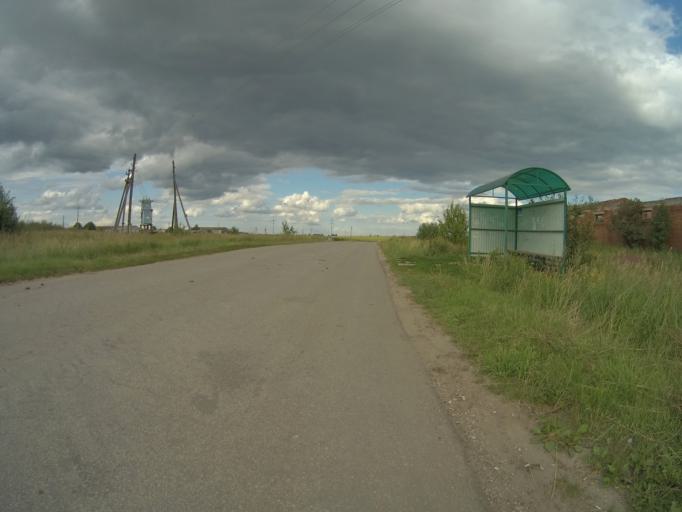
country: RU
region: Vladimir
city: Suzdal'
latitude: 56.3386
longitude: 40.4477
